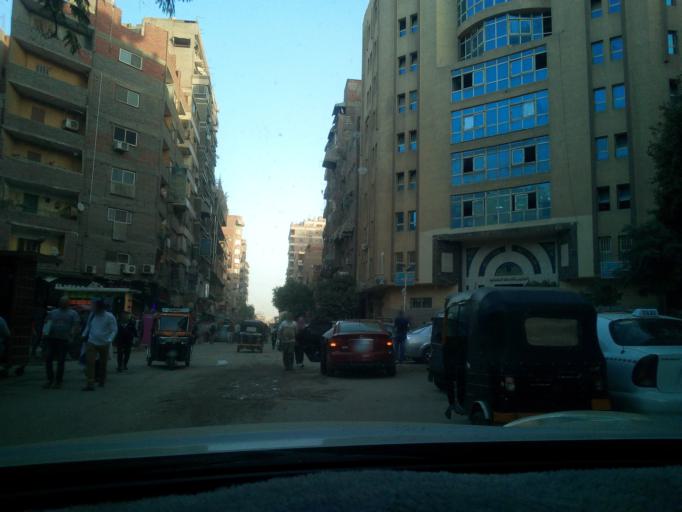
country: EG
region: Muhafazat al Qalyubiyah
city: Al Khankah
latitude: 30.1283
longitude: 31.3484
